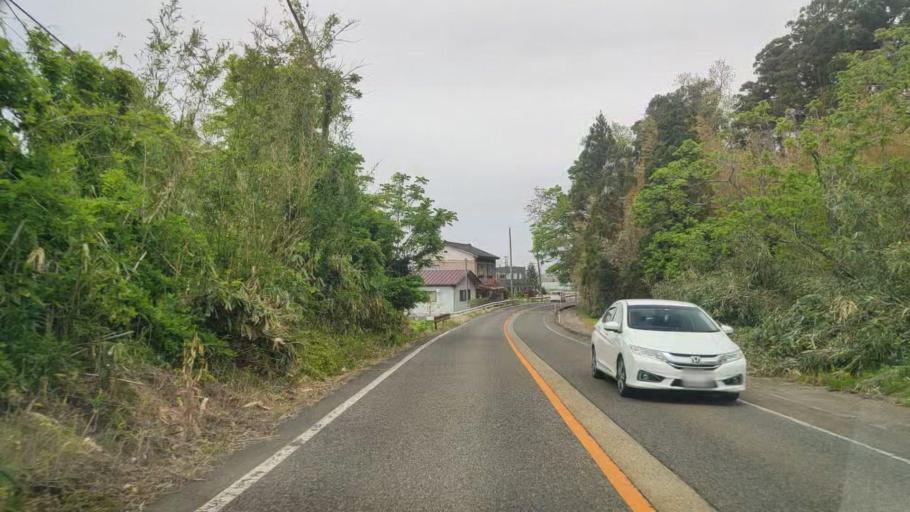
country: JP
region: Niigata
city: Shirone
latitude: 37.7303
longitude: 139.0815
